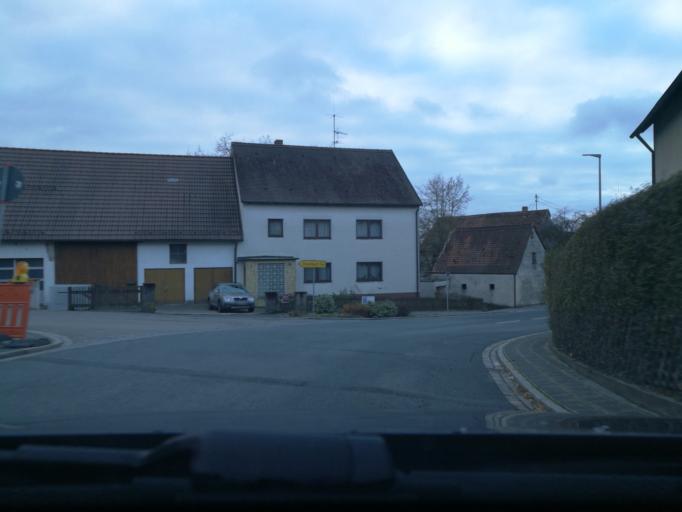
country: DE
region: Bavaria
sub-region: Regierungsbezirk Mittelfranken
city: Marloffstein
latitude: 49.6184
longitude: 11.0648
